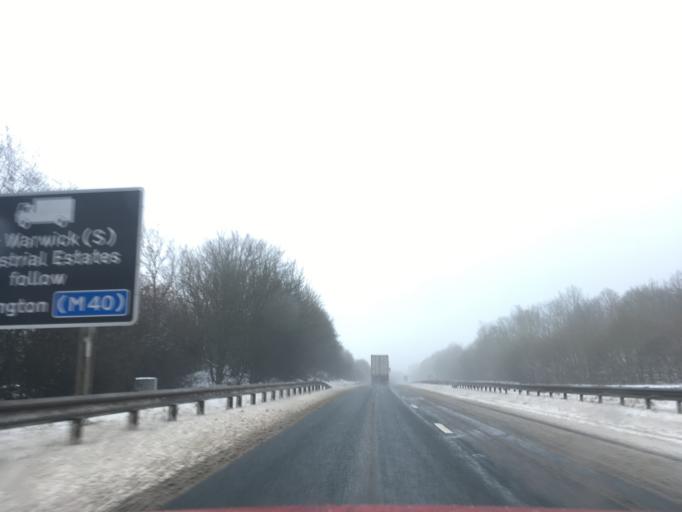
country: GB
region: England
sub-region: Warwickshire
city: Warwick
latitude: 52.2496
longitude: -1.6392
